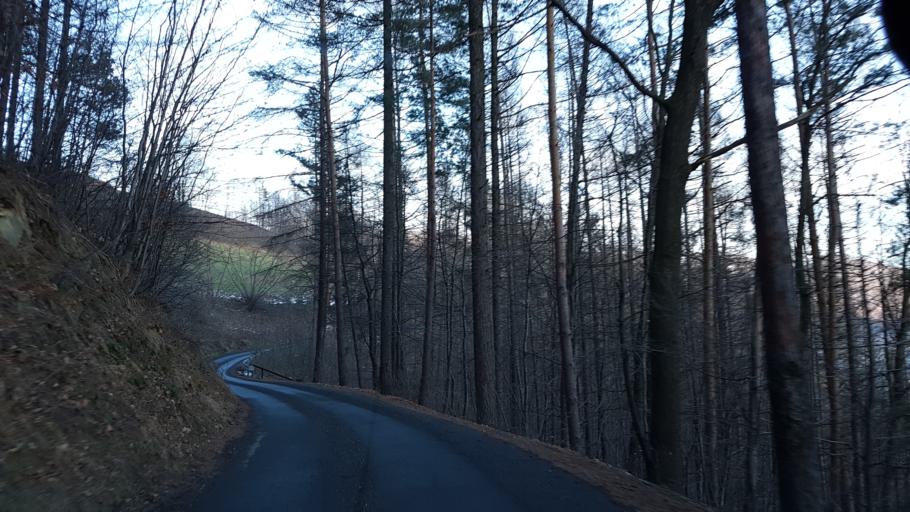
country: PL
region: Lesser Poland Voivodeship
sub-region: Powiat nowosadecki
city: Rytro
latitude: 49.4917
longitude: 20.6670
